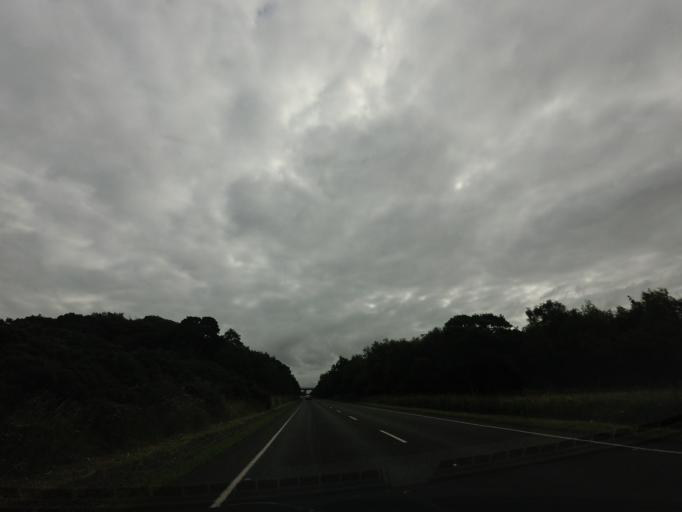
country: GB
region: Scotland
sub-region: Dumfries and Galloway
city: Gretna
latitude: 54.9923
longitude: -3.1355
